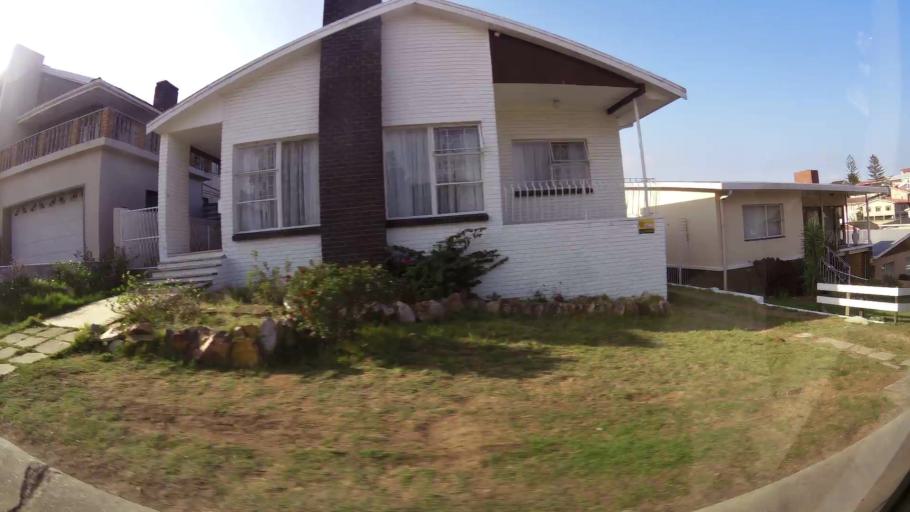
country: ZA
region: Eastern Cape
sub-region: Nelson Mandela Bay Metropolitan Municipality
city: Port Elizabeth
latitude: -33.9257
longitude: 25.5422
